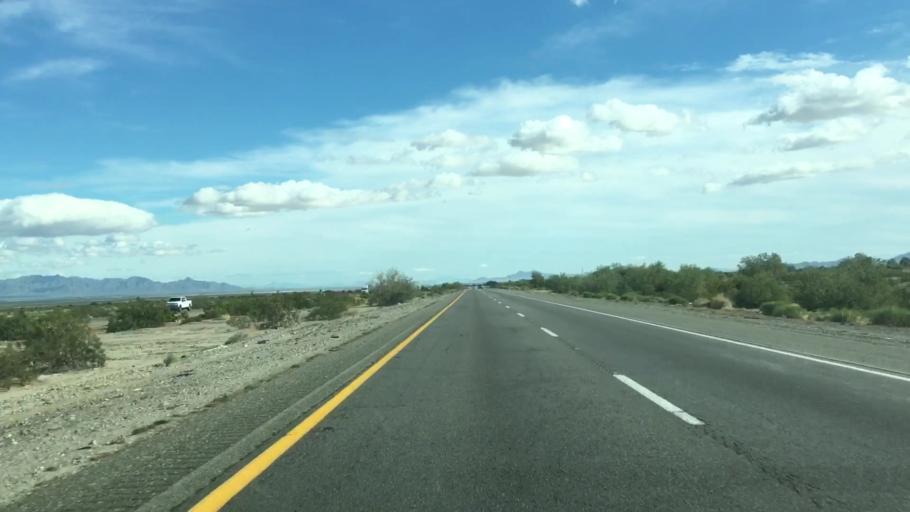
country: US
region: California
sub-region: Riverside County
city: Mesa Verde
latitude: 33.6609
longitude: -115.1713
